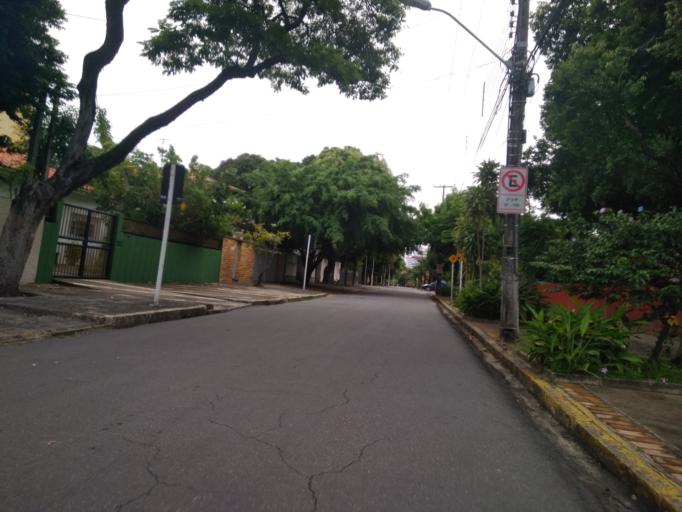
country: BR
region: Pernambuco
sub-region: Recife
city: Recife
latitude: -8.0324
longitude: -34.8860
